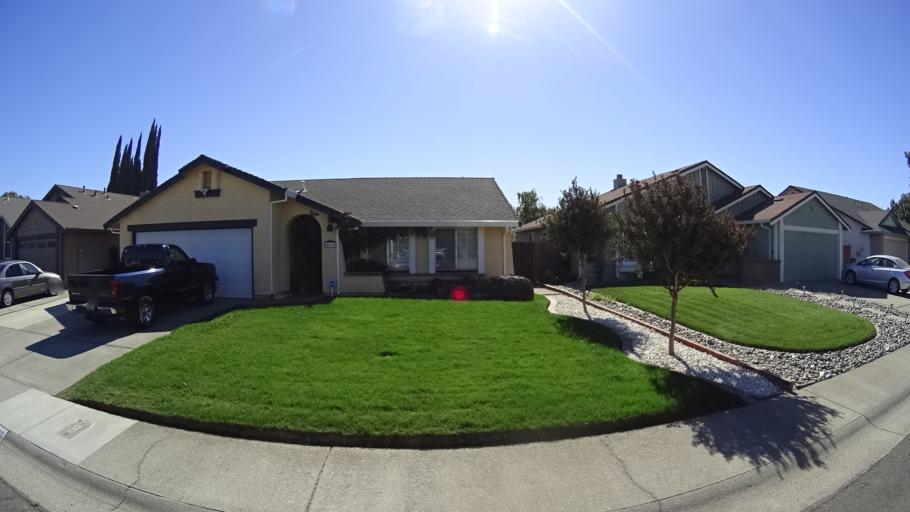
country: US
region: California
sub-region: Sacramento County
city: Parkway
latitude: 38.4681
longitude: -121.4588
